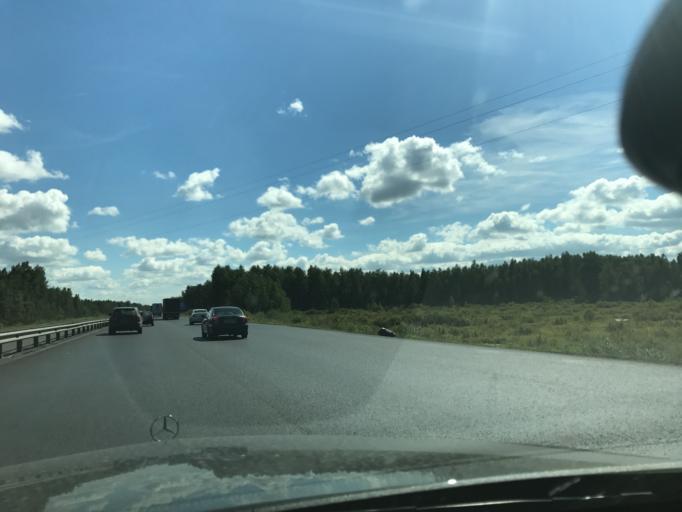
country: RU
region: Nizjnij Novgorod
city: Gorbatovka
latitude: 56.3009
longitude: 43.6888
